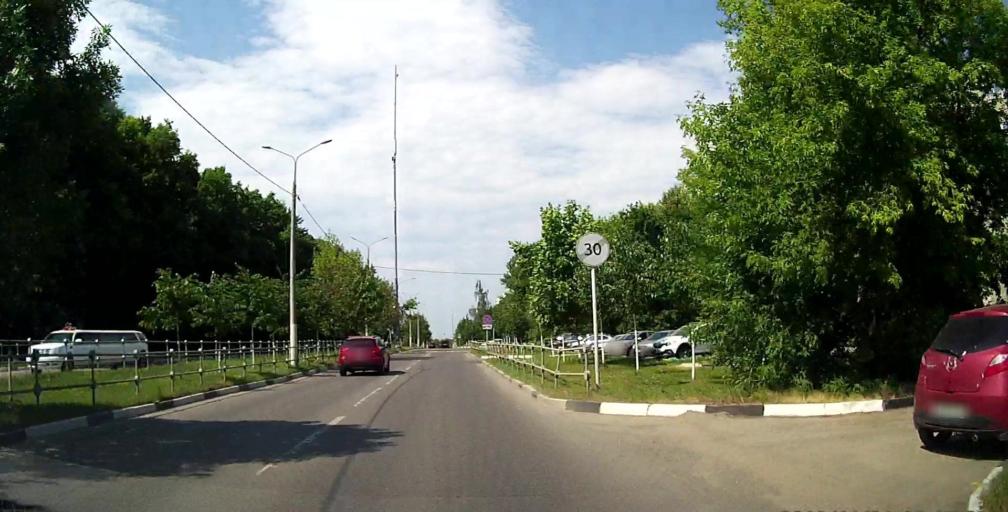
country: RU
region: Moskovskaya
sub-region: Podol'skiy Rayon
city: Podol'sk
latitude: 55.4149
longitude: 37.5217
